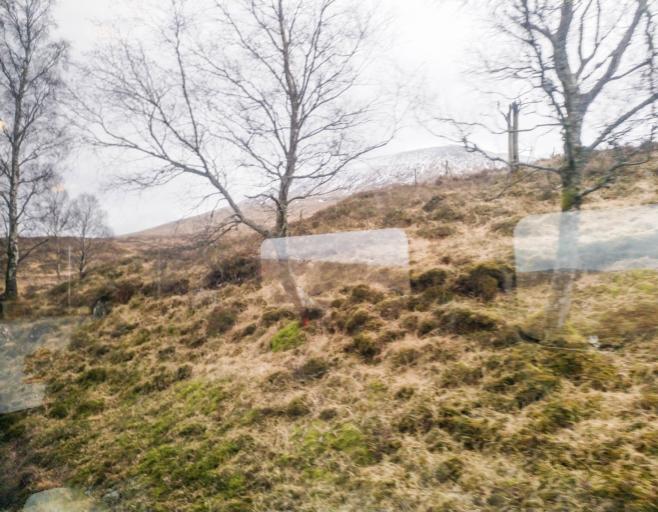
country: GB
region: Scotland
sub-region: Highland
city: Spean Bridge
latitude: 56.5835
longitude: -4.6718
